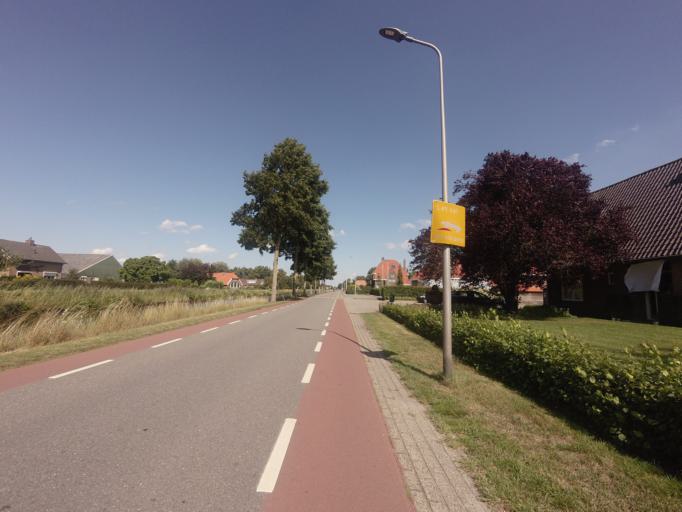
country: NL
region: Overijssel
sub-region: Gemeente Twenterand
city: Den Ham
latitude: 52.5639
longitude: 6.4329
